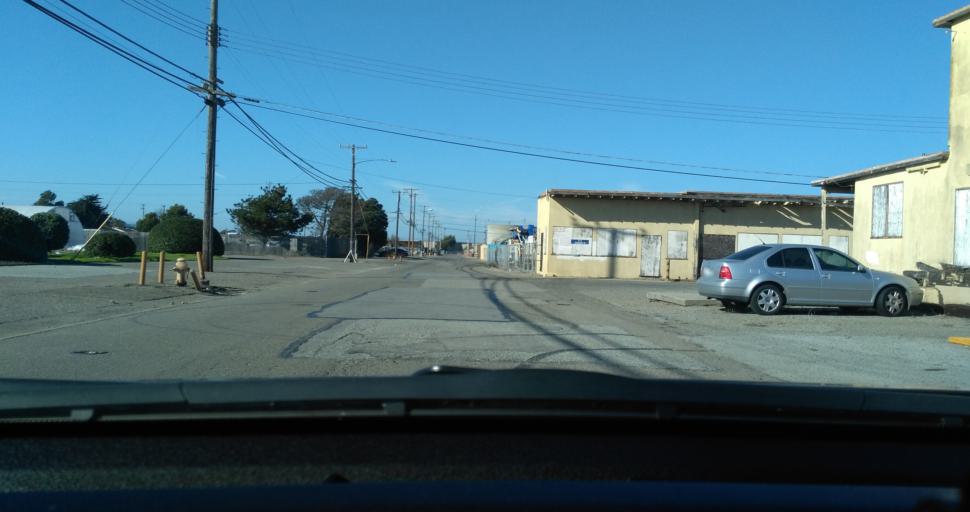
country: US
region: California
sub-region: San Francisco County
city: San Francisco
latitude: 37.8273
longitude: -122.3683
